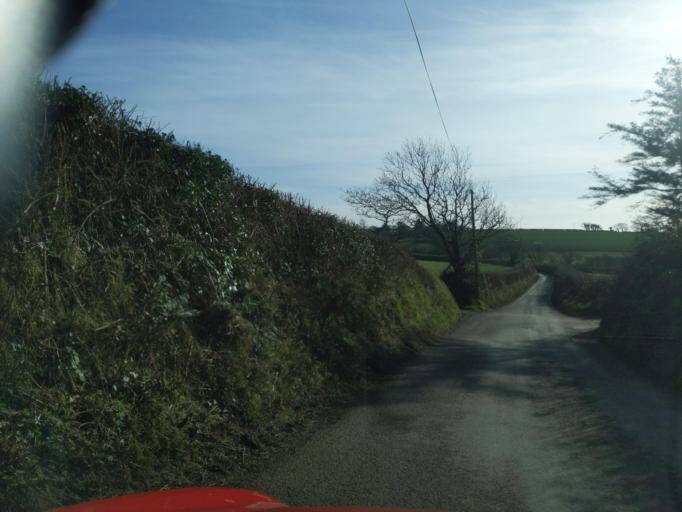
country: GB
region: England
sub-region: Devon
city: Kingsbridge
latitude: 50.3340
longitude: -3.7199
